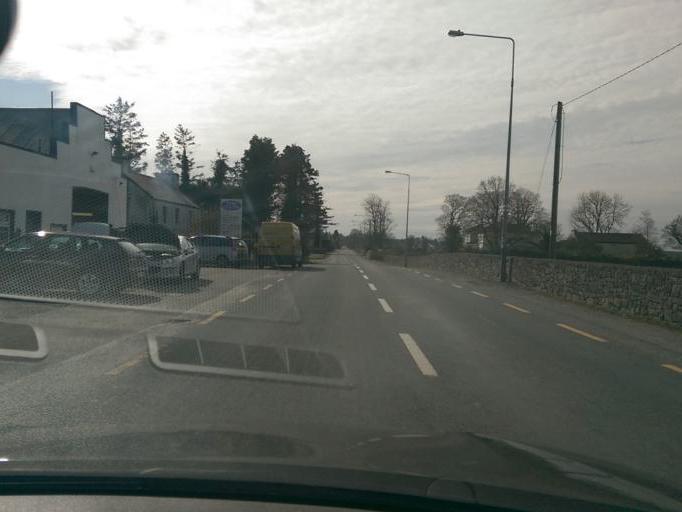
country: IE
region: Connaught
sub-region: County Galway
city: Tuam
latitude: 53.4358
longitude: -8.7517
